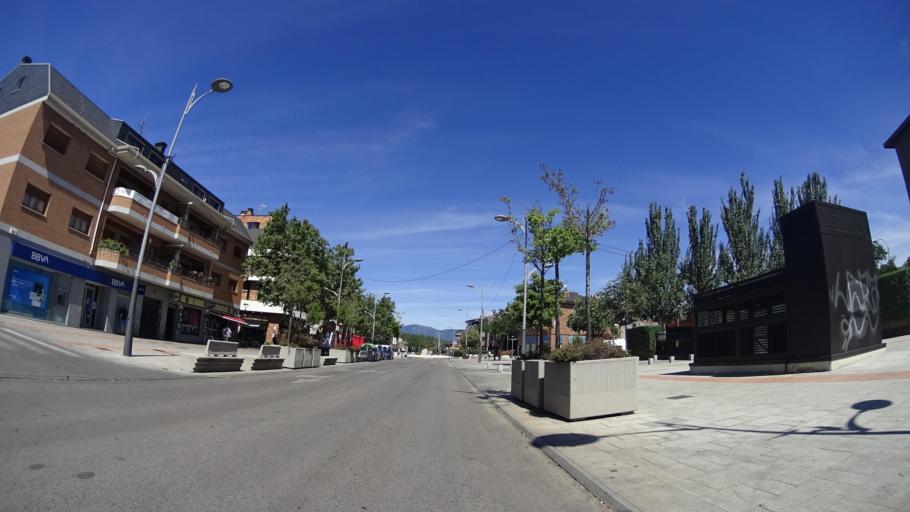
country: ES
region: Madrid
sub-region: Provincia de Madrid
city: Collado-Villalba
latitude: 40.6318
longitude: -4.0071
